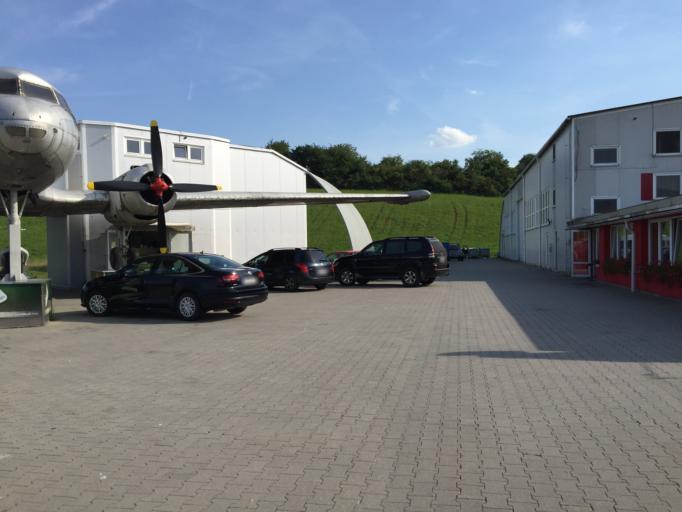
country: SK
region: Presovsky
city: Giraltovce
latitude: 49.0356
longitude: 21.4615
